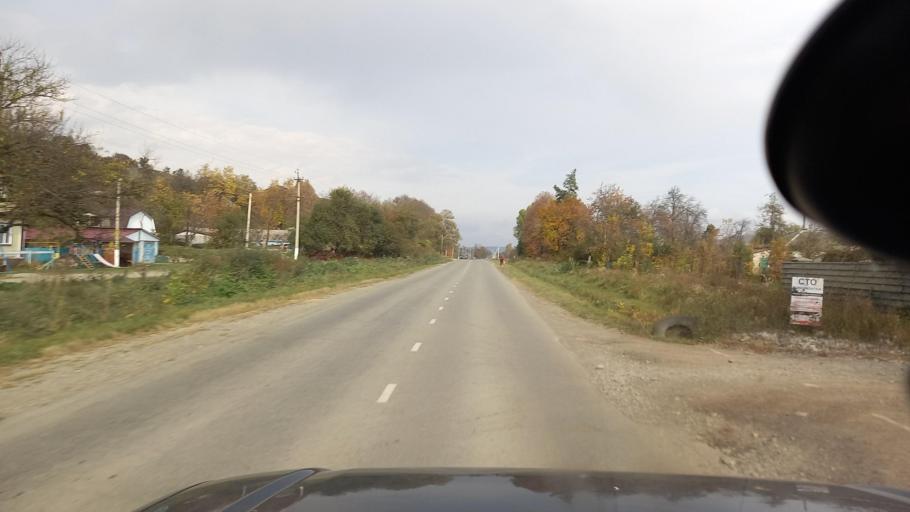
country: RU
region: Krasnodarskiy
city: Psebay
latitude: 44.1331
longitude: 40.8133
